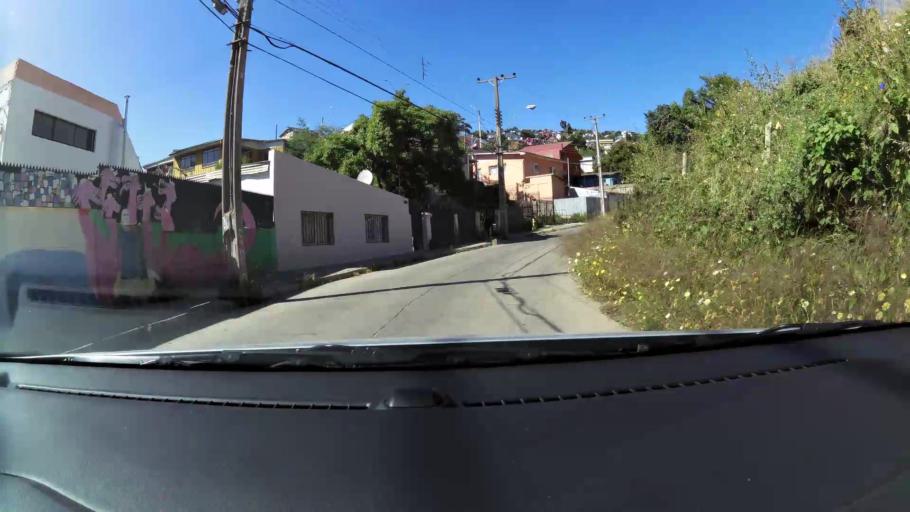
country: CL
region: Valparaiso
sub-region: Provincia de Valparaiso
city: Valparaiso
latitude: -33.0623
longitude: -71.5914
